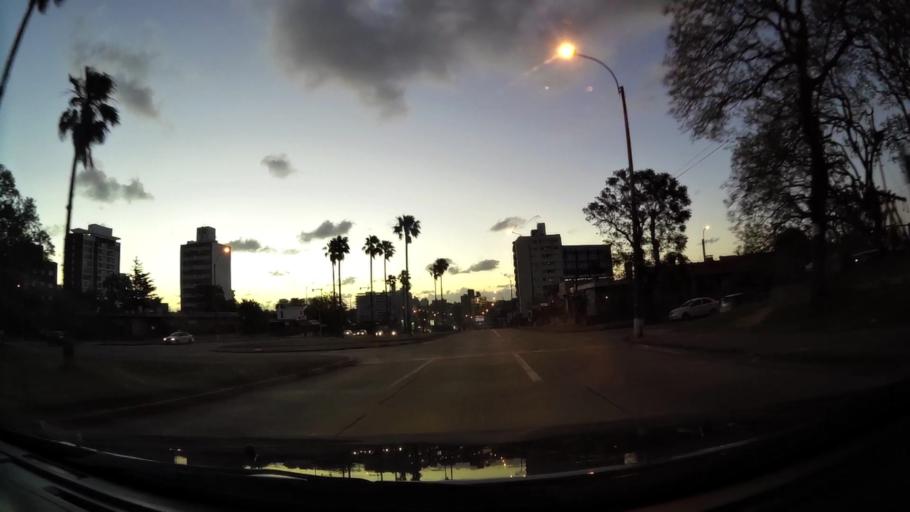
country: UY
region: Canelones
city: Paso de Carrasco
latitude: -34.8858
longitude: -56.1013
